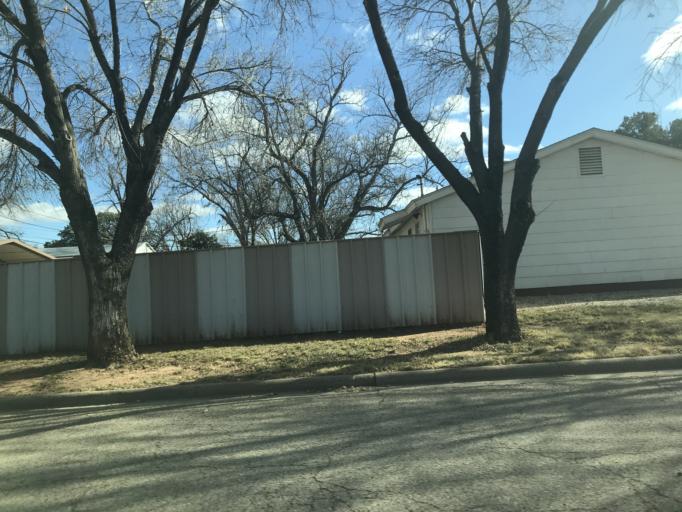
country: US
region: Texas
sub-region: Taylor County
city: Abilene
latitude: 32.4612
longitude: -99.7697
